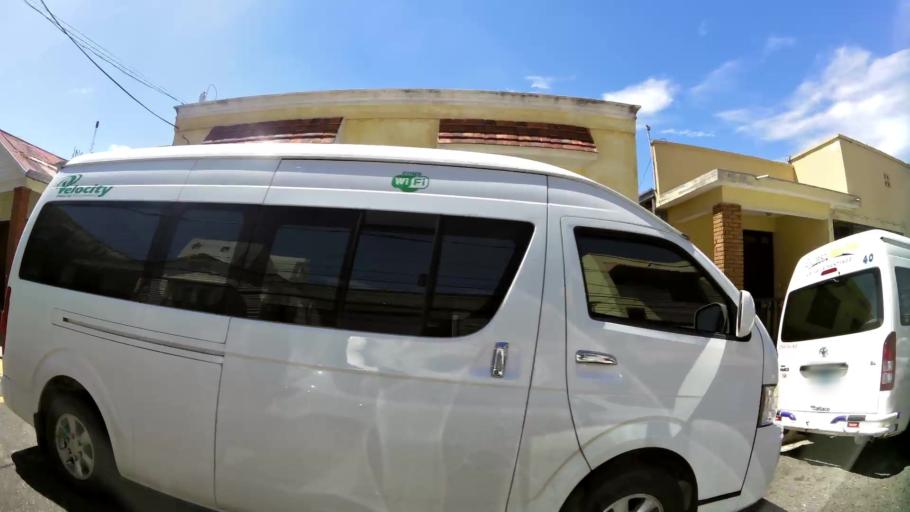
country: DO
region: Santiago
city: Santiago de los Caballeros
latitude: 19.4515
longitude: -70.6986
